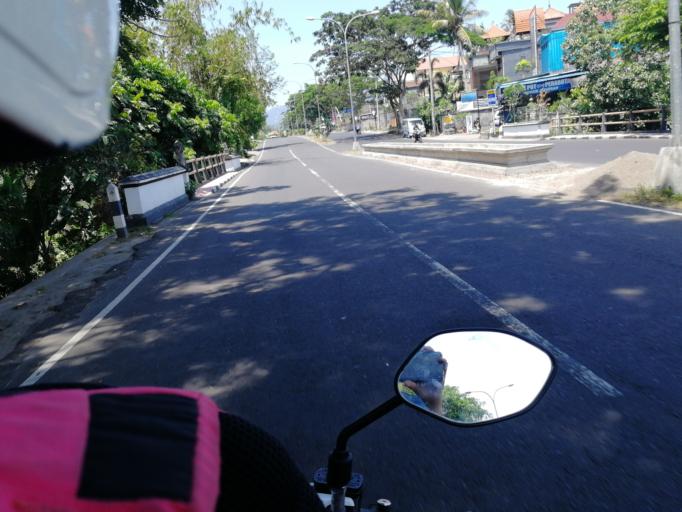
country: ID
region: Bali
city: Subagan
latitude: -8.4409
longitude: 115.5918
